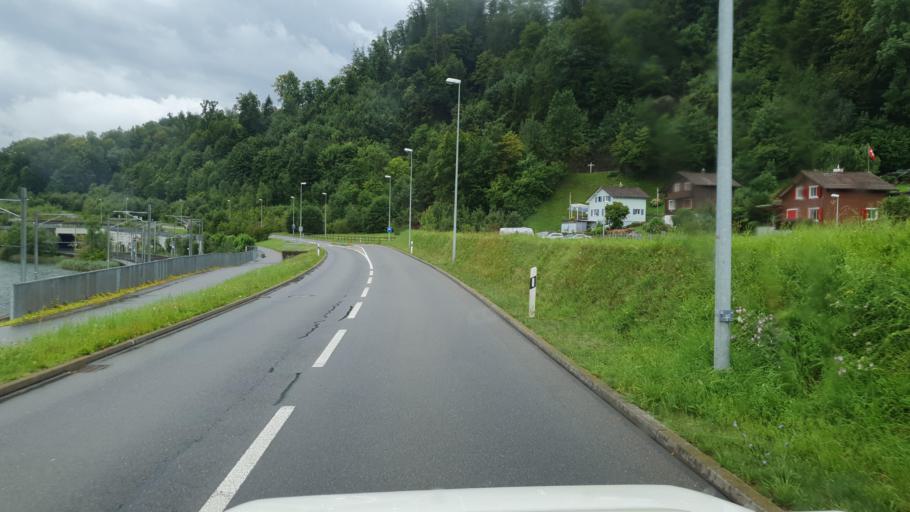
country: CH
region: Lucerne
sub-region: Lucerne-Land District
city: Horw
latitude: 47.0072
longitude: 8.3050
